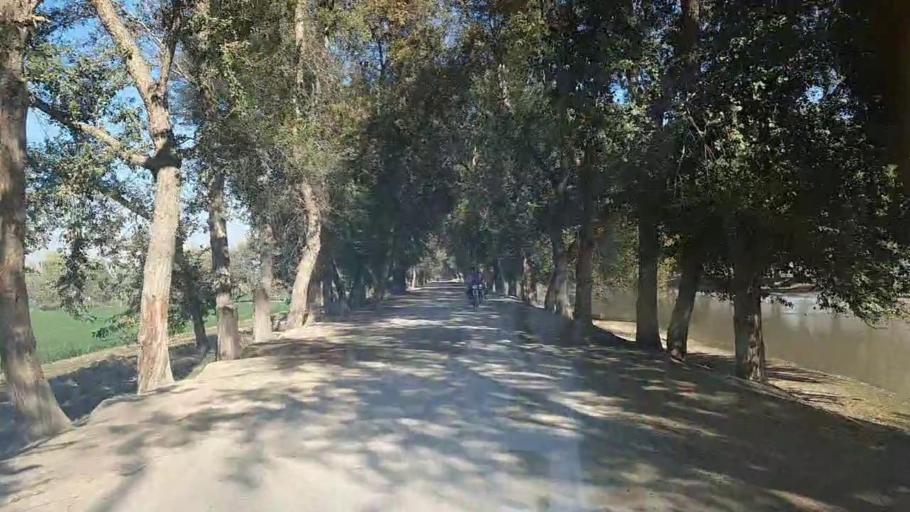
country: PK
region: Sindh
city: Khairpur
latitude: 27.9989
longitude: 69.6523
